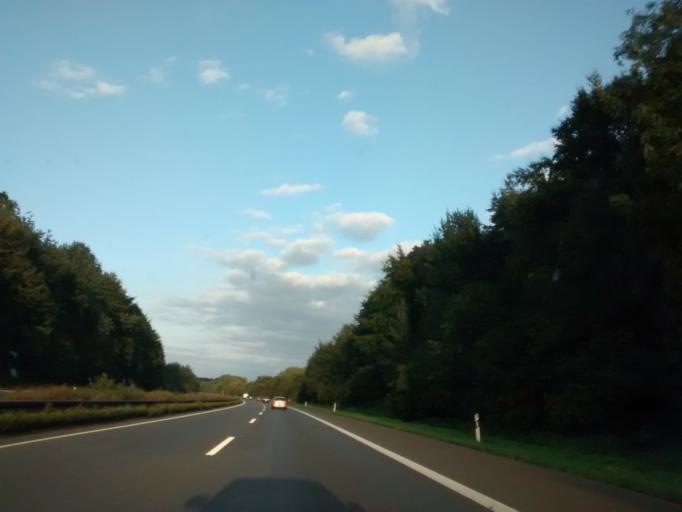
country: DE
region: North Rhine-Westphalia
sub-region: Regierungsbezirk Munster
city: Tecklenburg
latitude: 52.2523
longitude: 7.8067
